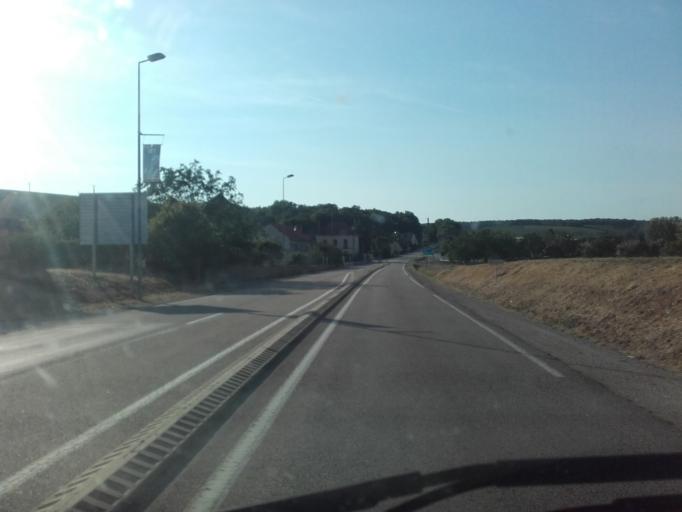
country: FR
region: Bourgogne
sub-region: Departement de l'Yonne
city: Chablis
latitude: 47.8203
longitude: 3.7776
